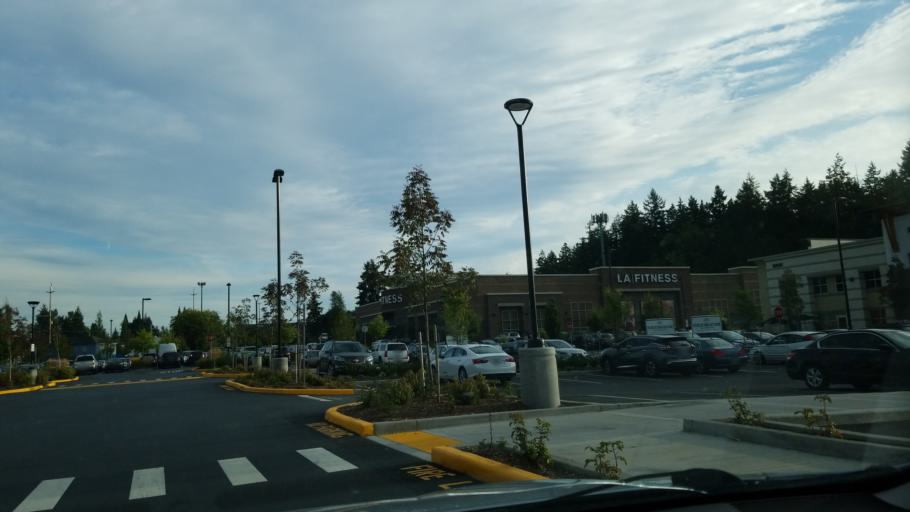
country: US
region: Washington
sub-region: Snohomish County
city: Lynnwood
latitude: 47.8204
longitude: -122.3179
